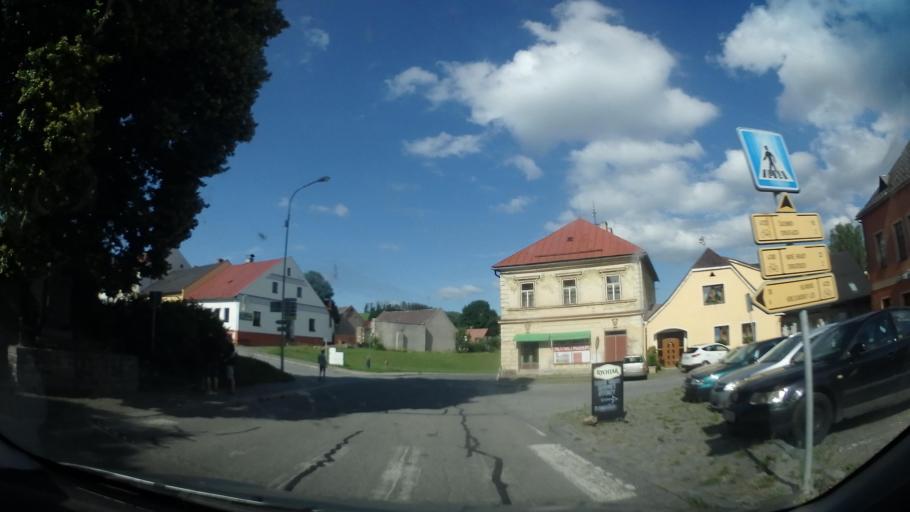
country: CZ
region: Vysocina
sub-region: Okres Zd'ar nad Sazavou
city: Svratka
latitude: 49.7109
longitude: 16.0315
